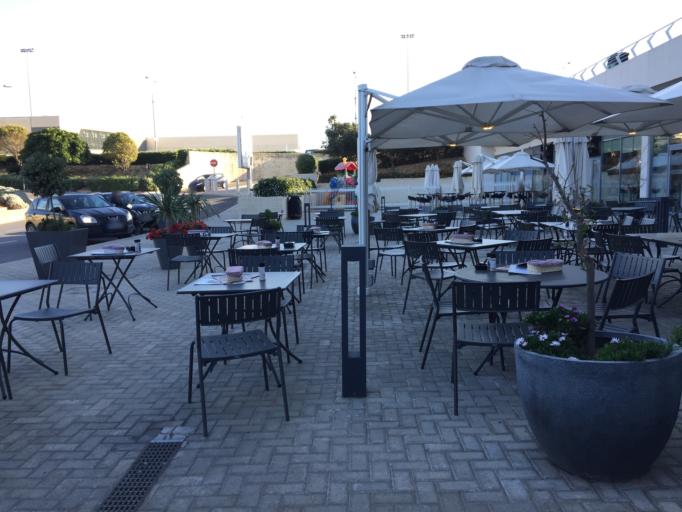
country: MT
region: Il-Gudja
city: Gudja
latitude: 35.8511
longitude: 14.4948
